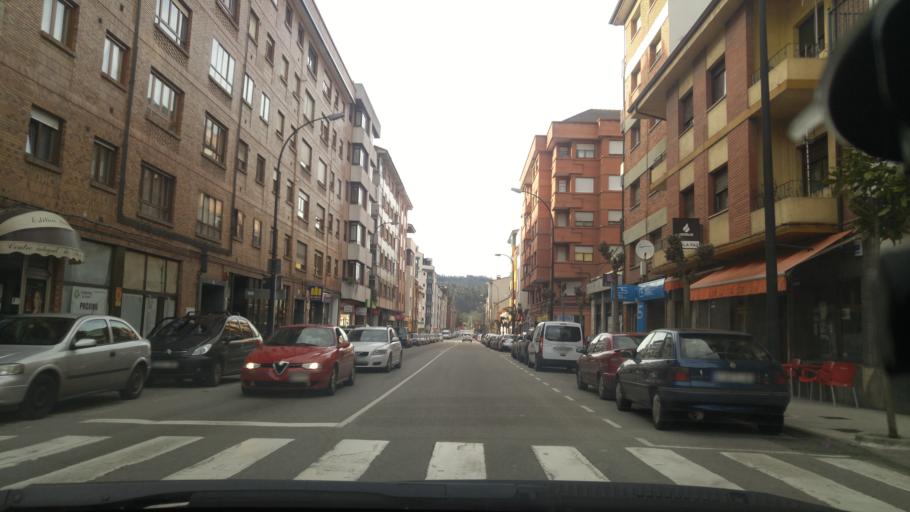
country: ES
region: Asturias
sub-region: Province of Asturias
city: Llanera
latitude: 43.4402
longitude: -5.8519
